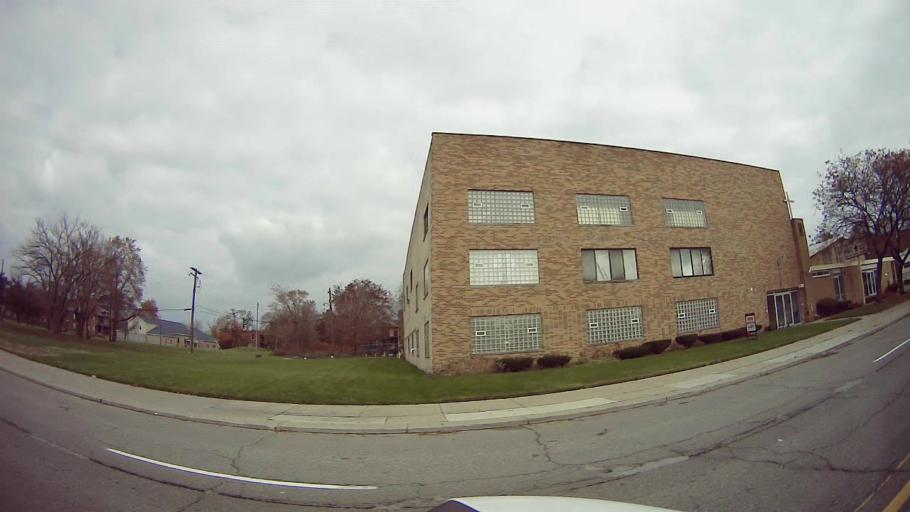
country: US
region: Michigan
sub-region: Wayne County
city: Highland Park
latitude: 42.3585
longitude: -83.0984
